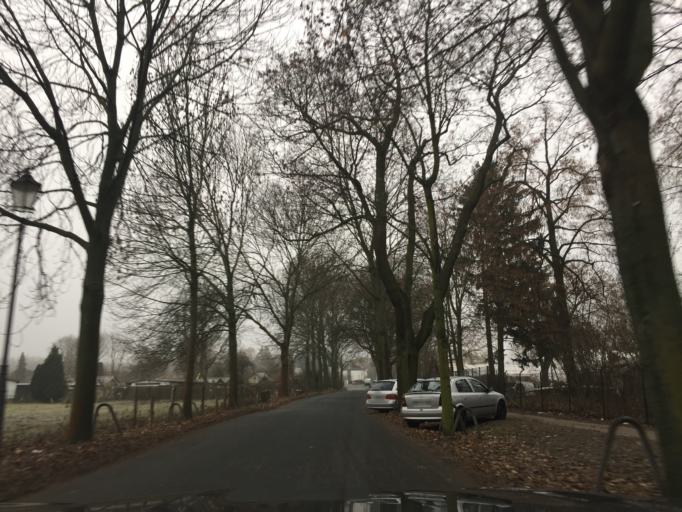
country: DE
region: Berlin
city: Spandau
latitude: 52.5252
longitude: 13.2094
